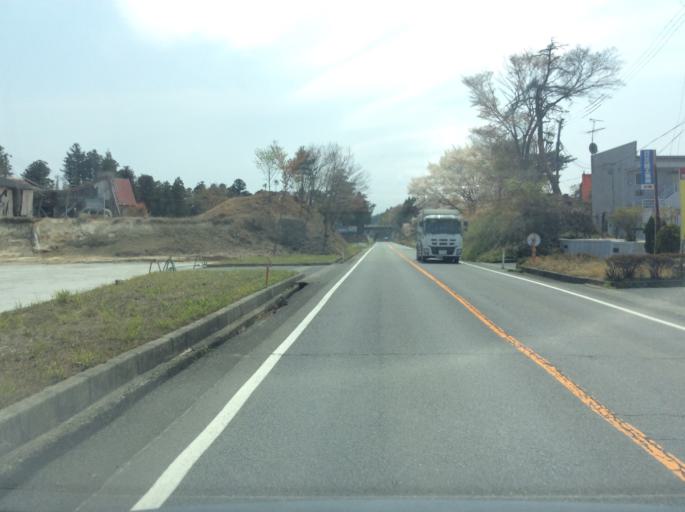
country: JP
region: Fukushima
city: Namie
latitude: 37.3509
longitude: 141.0113
